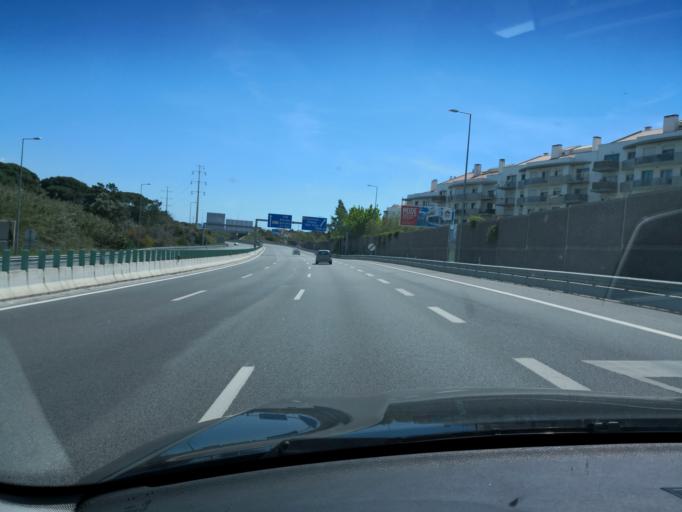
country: PT
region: Setubal
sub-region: Almada
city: Sobreda
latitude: 38.6442
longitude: -9.2017
